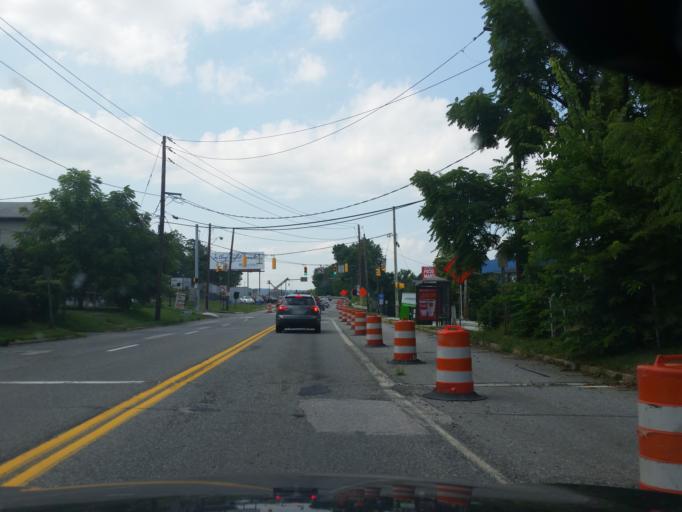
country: US
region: Pennsylvania
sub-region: Cumberland County
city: West Fairview
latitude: 40.2730
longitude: -76.9161
